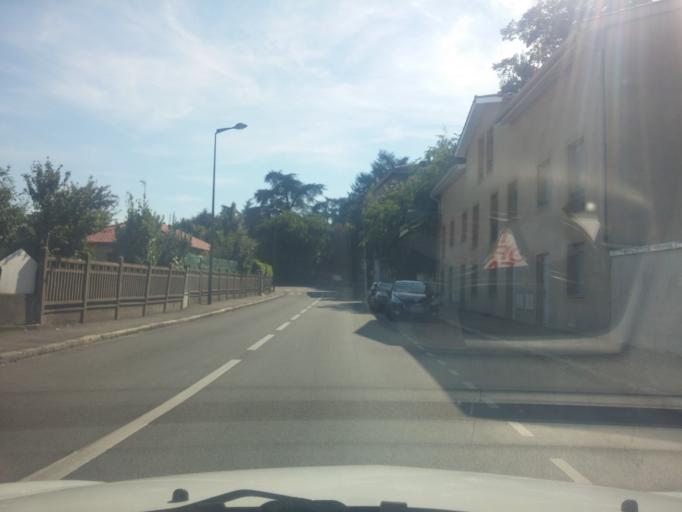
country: FR
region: Rhone-Alpes
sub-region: Departement du Rhone
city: Sainte-Foy-les-Lyon
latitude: 45.7336
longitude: 4.8030
